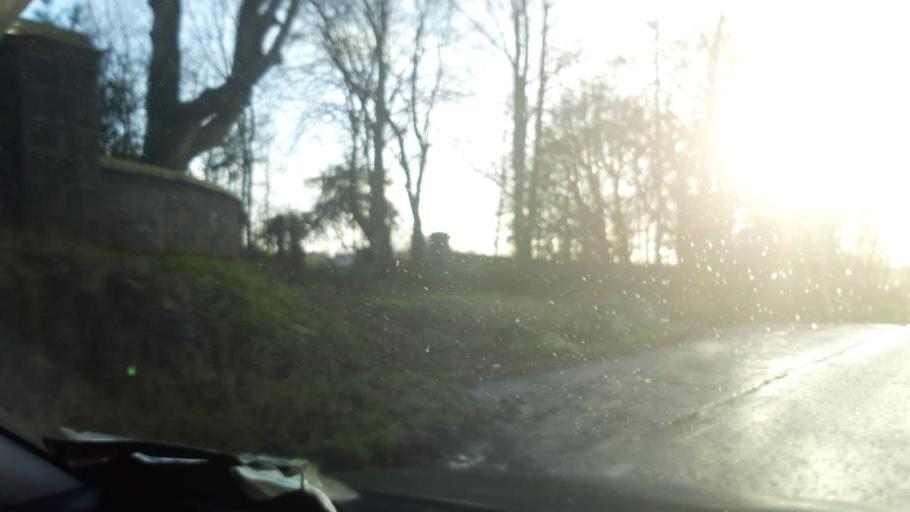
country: GB
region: Northern Ireland
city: Maghera
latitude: 54.8345
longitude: -6.6827
